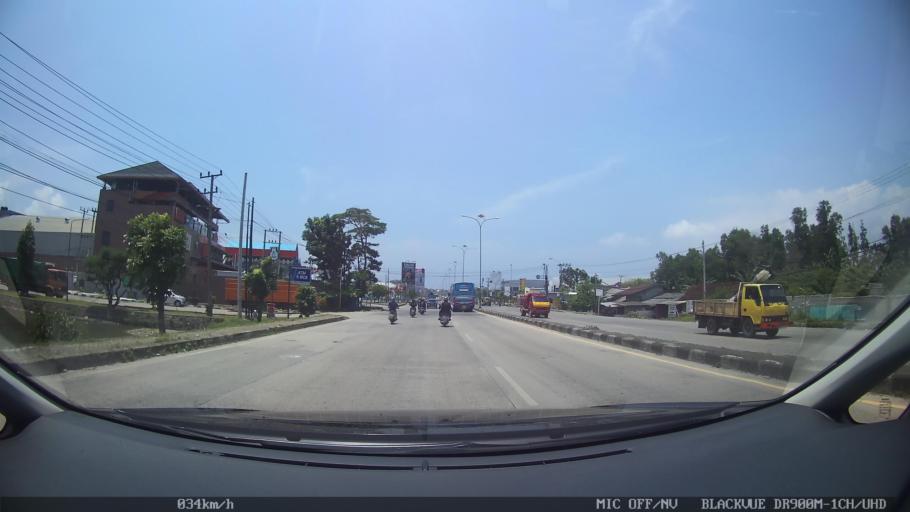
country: ID
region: Lampung
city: Kedaton
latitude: -5.3885
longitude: 105.2879
